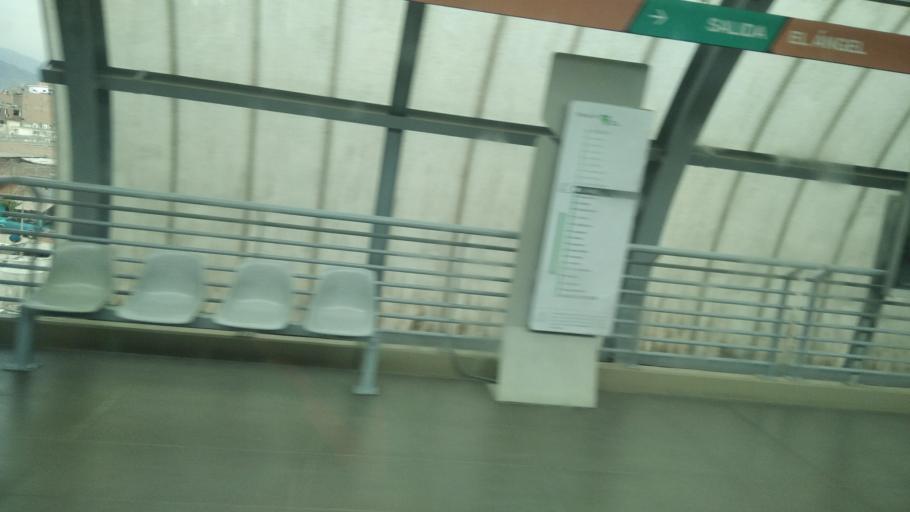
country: PE
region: Lima
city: Lima
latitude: -12.0461
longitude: -77.0097
